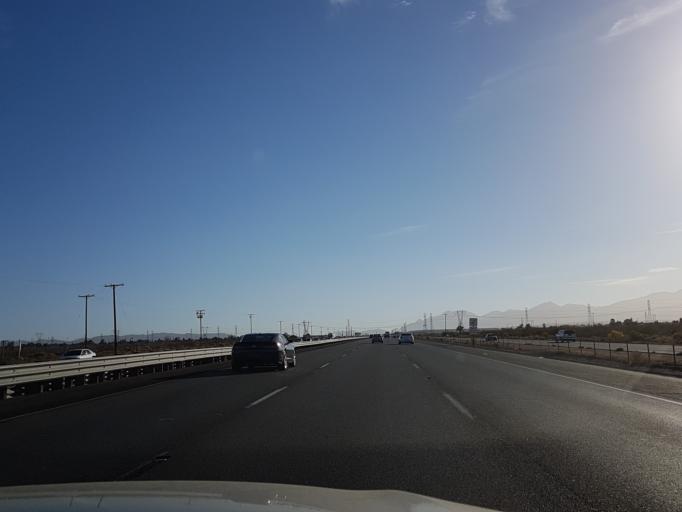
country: US
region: California
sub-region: San Bernardino County
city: Mountain View Acres
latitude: 34.4550
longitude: -117.3585
